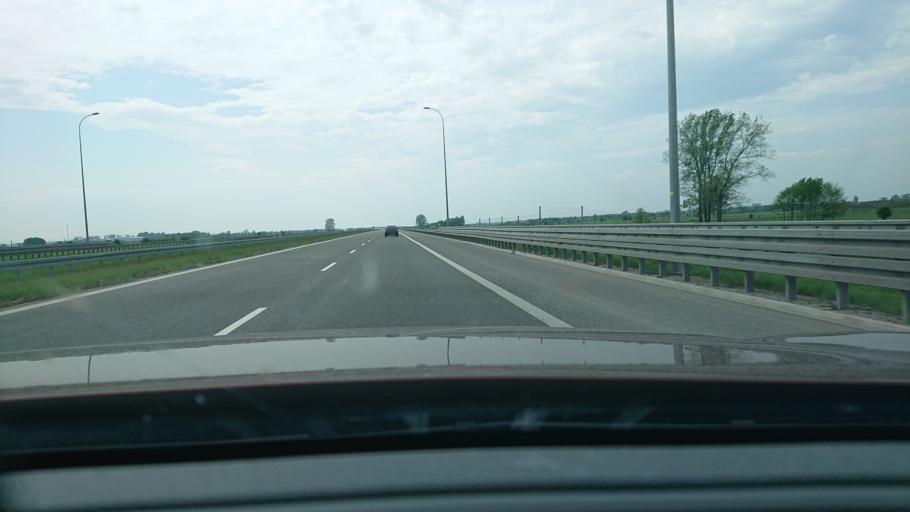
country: PL
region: Subcarpathian Voivodeship
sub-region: Powiat rzeszowski
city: Wolka Podlesna
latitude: 50.0937
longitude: 22.1415
